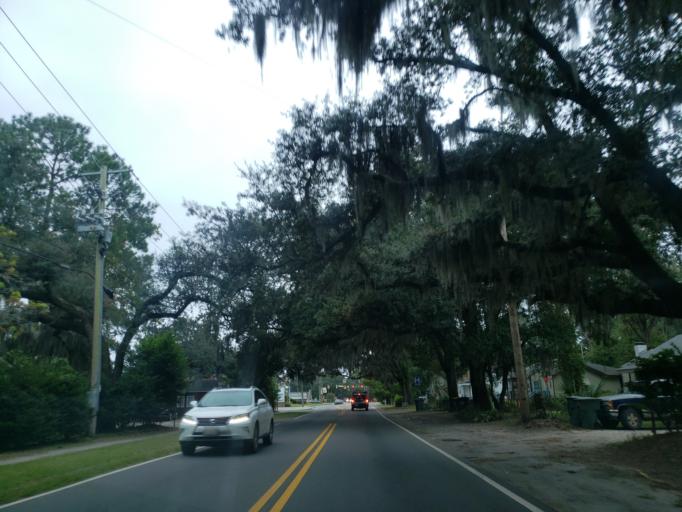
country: US
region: Georgia
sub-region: Chatham County
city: Thunderbolt
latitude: 32.0211
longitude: -81.0742
